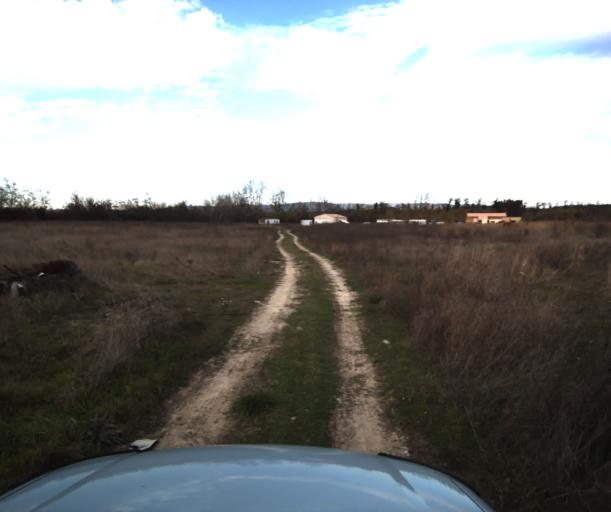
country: FR
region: Provence-Alpes-Cote d'Azur
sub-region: Departement des Bouches-du-Rhone
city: Meyrargues
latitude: 43.6651
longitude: 5.5227
